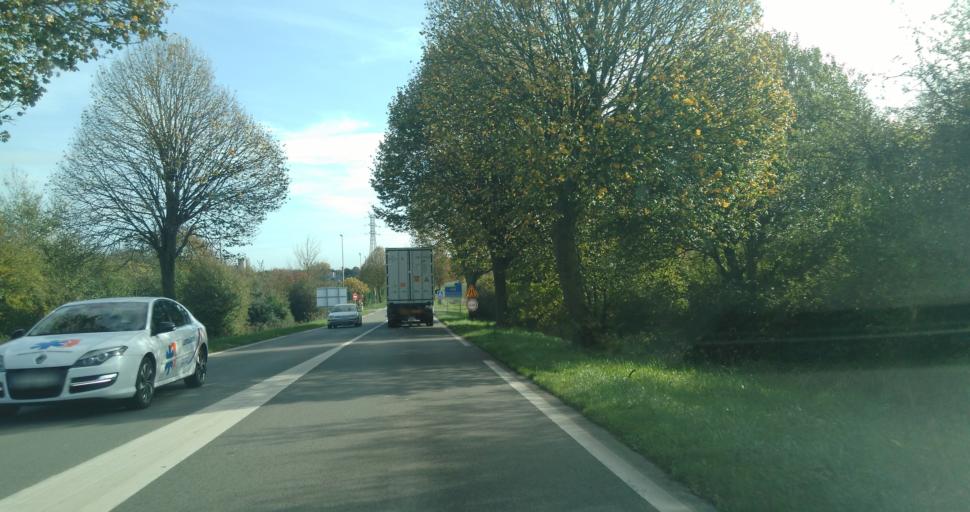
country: FR
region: Nord-Pas-de-Calais
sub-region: Departement du Pas-de-Calais
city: Hesdin
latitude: 50.3670
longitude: 2.0319
